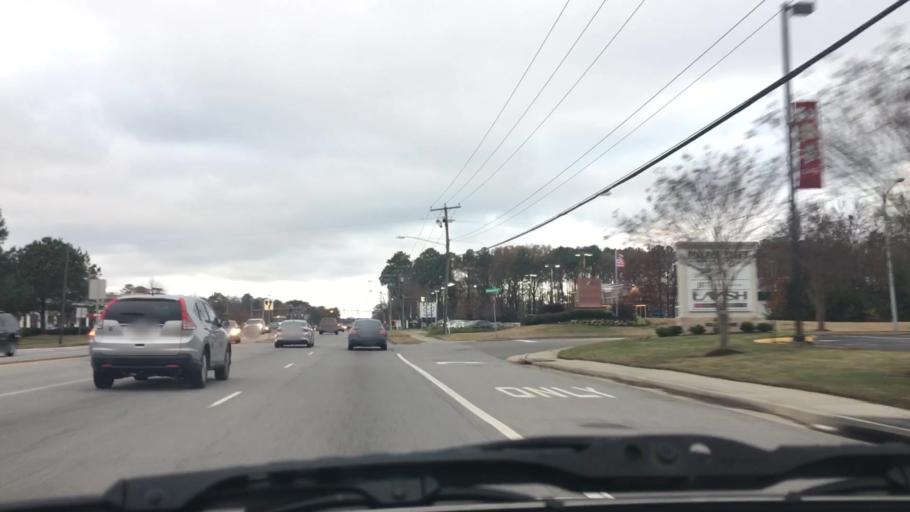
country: US
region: Virginia
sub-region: City of Virginia Beach
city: Virginia Beach
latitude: 36.8220
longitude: -76.1242
